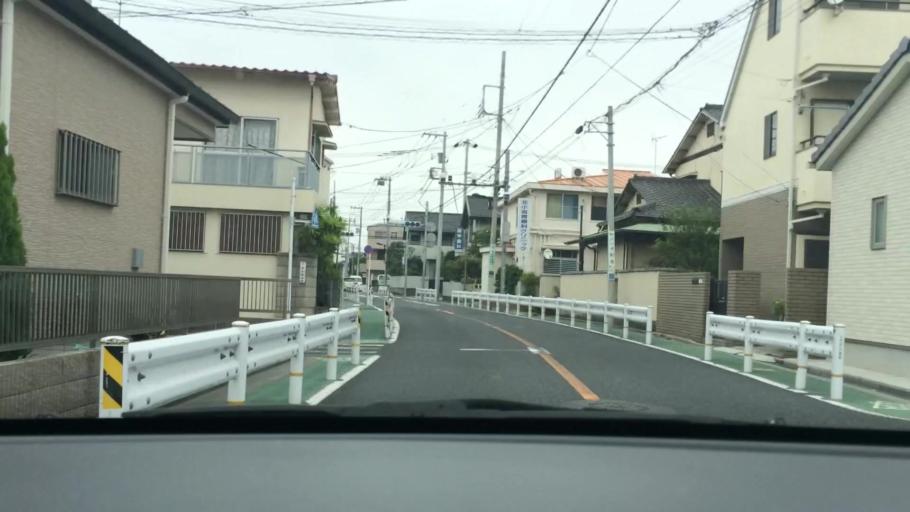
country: JP
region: Chiba
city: Matsudo
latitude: 35.7416
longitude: 139.8919
